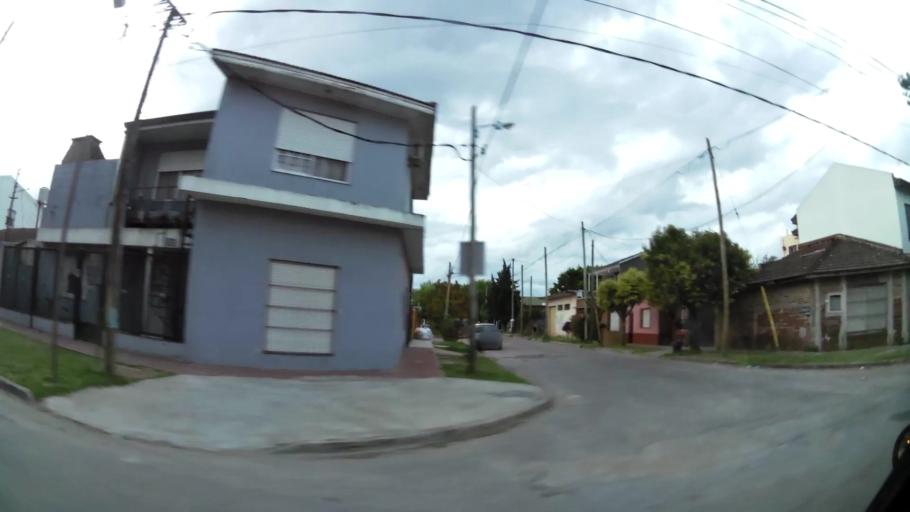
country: AR
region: Buenos Aires
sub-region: Partido de Quilmes
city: Quilmes
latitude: -34.7356
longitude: -58.2308
